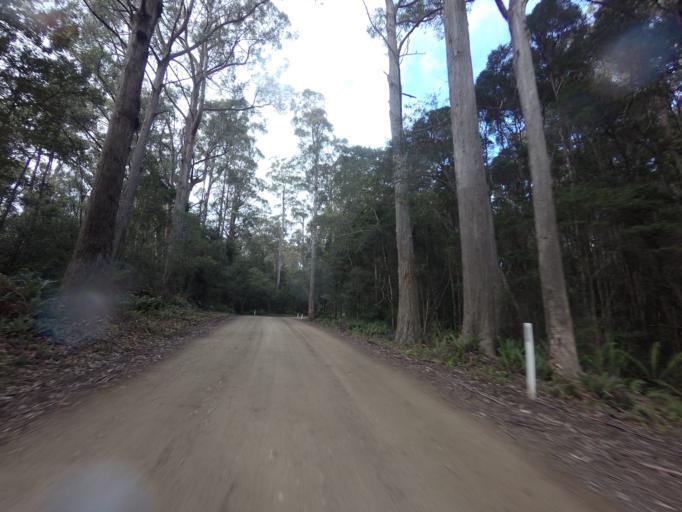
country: AU
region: Tasmania
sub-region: Huon Valley
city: Geeveston
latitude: -43.5691
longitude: 146.8897
